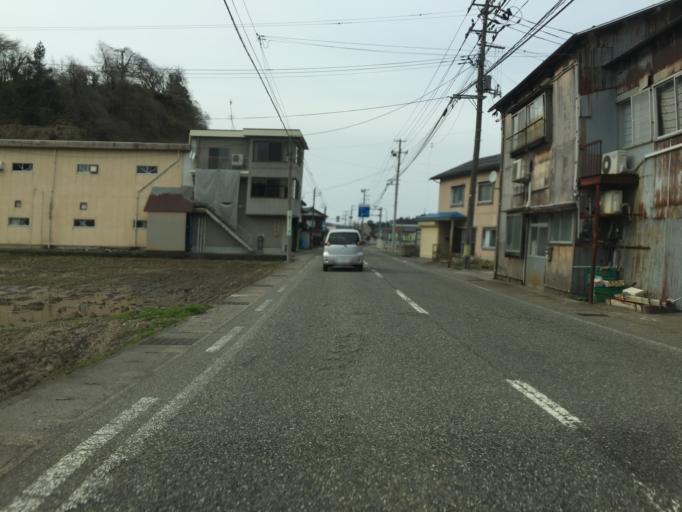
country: JP
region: Niigata
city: Tochio-honcho
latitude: 37.4648
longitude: 139.0047
